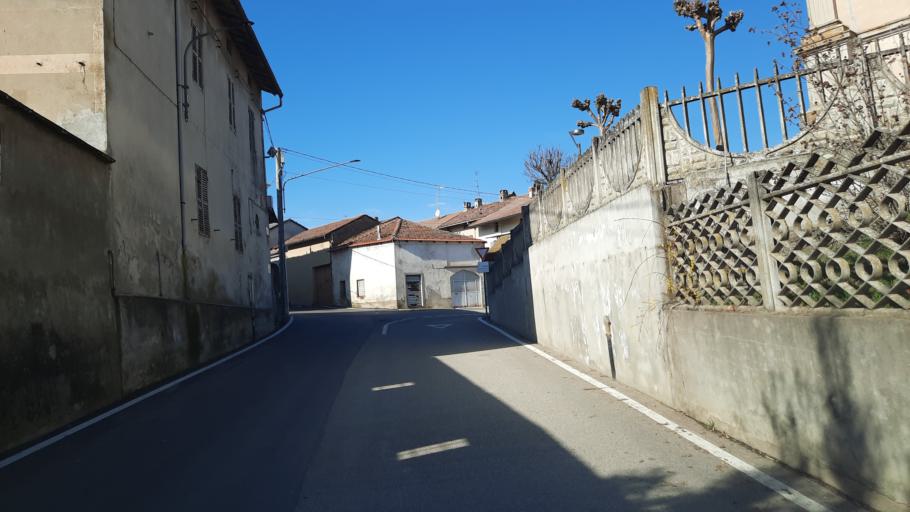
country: IT
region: Piedmont
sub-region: Provincia di Vercelli
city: Rive
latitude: 45.2120
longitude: 8.4186
